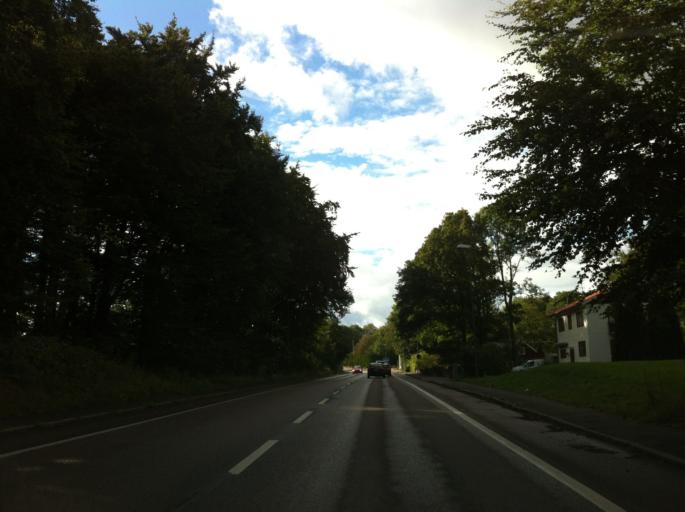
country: SE
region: Skane
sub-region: Hassleholms Kommun
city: Tormestorp
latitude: 56.1627
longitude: 13.5943
